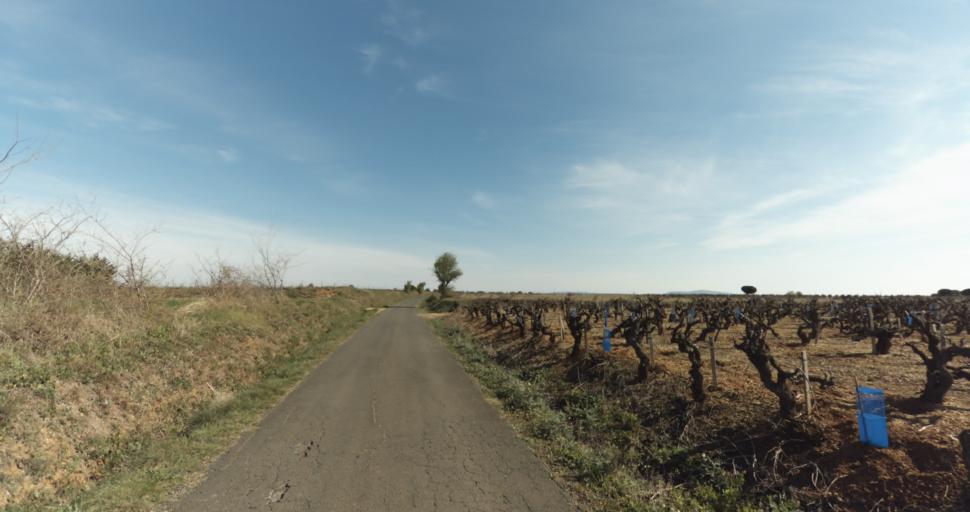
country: FR
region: Languedoc-Roussillon
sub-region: Departement de l'Herault
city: Marseillan
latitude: 43.3421
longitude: 3.5185
